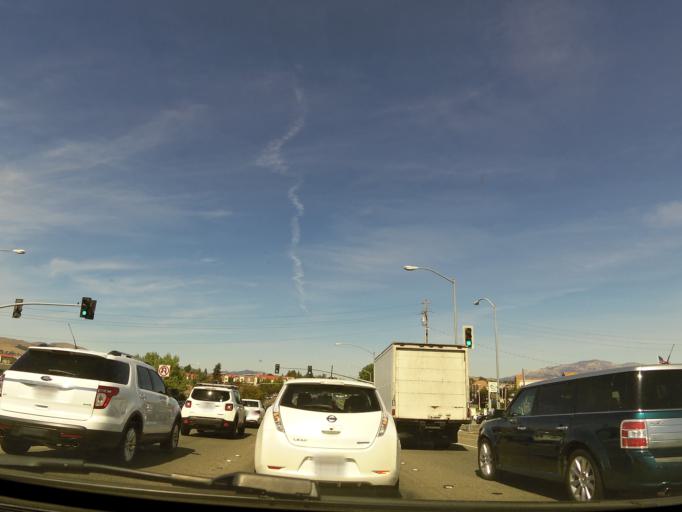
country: US
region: California
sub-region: Alameda County
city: Dublin
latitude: 37.7028
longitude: -121.9078
